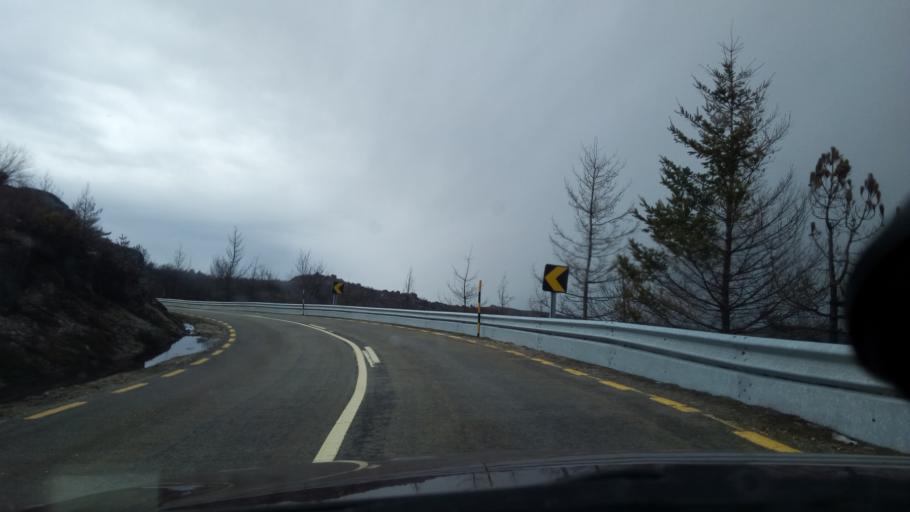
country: PT
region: Guarda
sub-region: Manteigas
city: Manteigas
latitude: 40.4153
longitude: -7.5821
